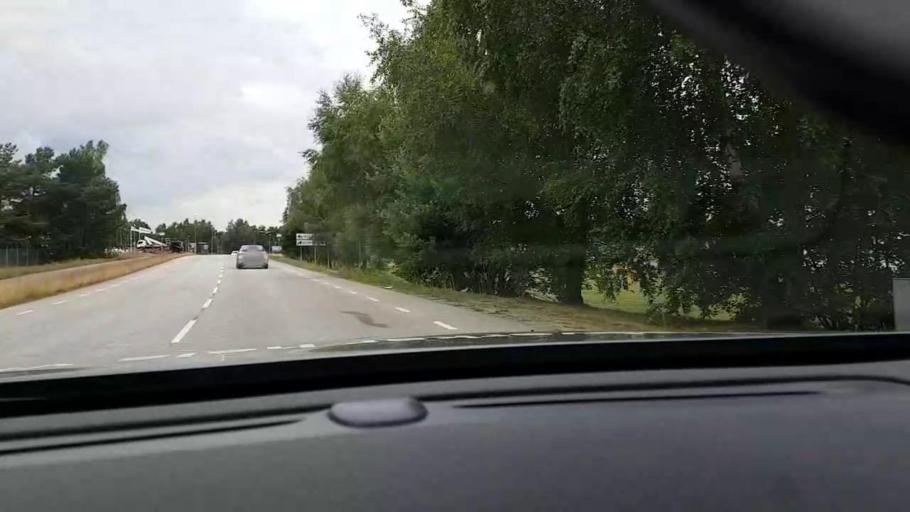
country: SE
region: Skane
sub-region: Hassleholms Kommun
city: Hassleholm
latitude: 56.1668
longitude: 13.8042
